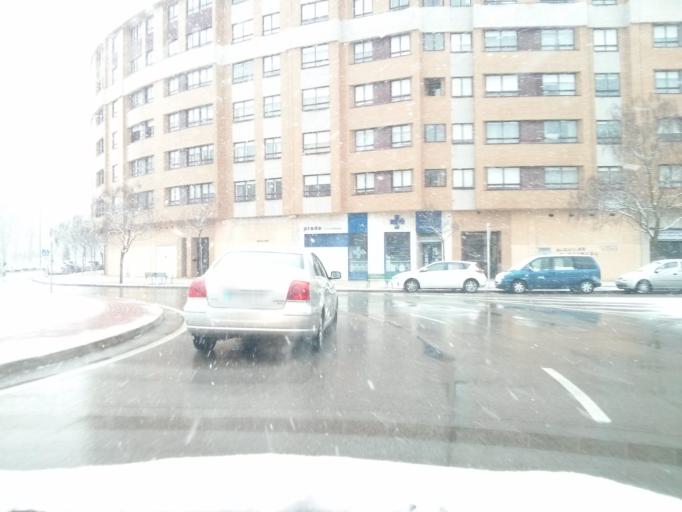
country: ES
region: Castille and Leon
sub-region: Provincia de Burgos
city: Burgos
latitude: 42.3538
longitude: -3.6812
